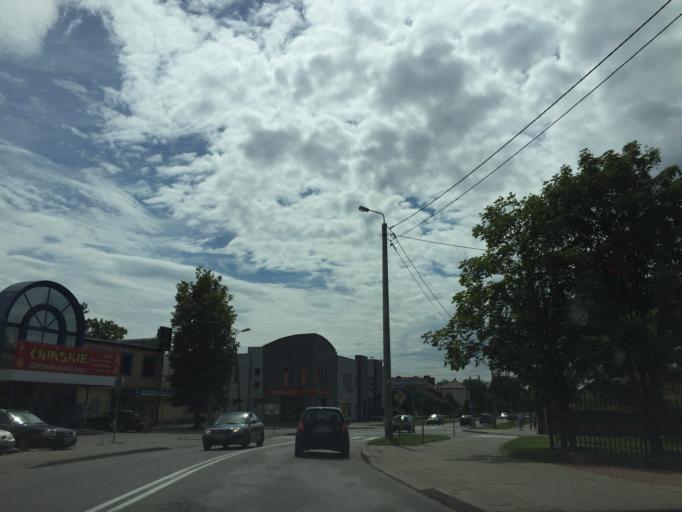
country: PL
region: Podlasie
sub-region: Powiat bielski
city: Bielsk Podlaski
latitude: 52.7634
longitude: 23.1859
